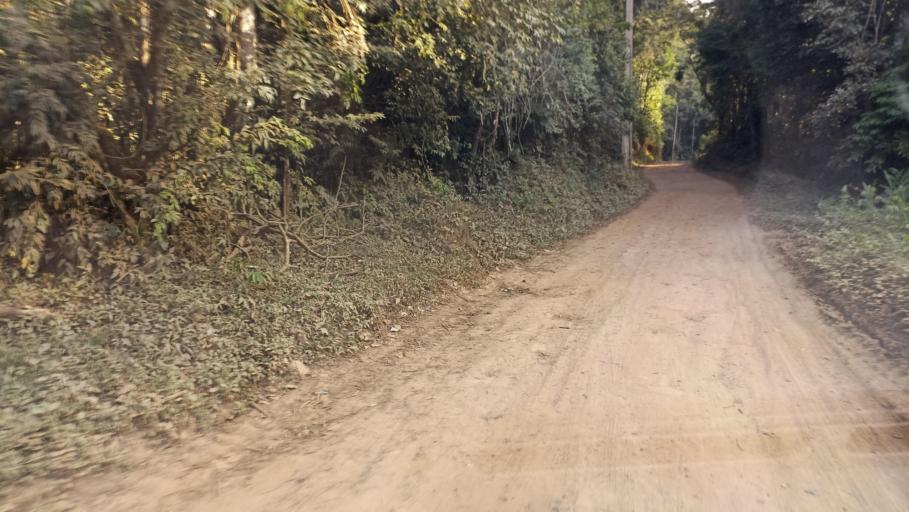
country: BR
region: Minas Gerais
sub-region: Ouro Preto
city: Ouro Preto
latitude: -20.3014
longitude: -43.5748
